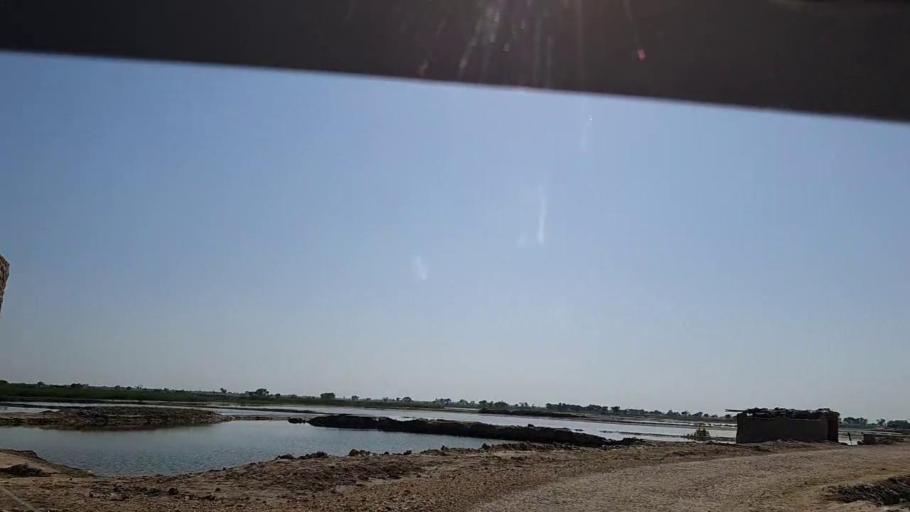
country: PK
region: Sindh
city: Tangwani
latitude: 28.3171
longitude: 69.0883
